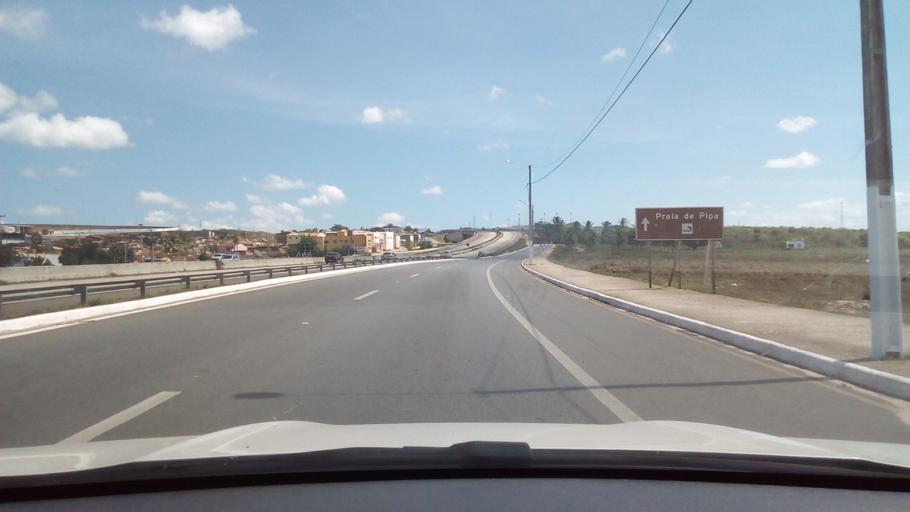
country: BR
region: Rio Grande do Norte
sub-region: Goianinha
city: Goianinha
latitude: -6.2721
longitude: -35.2082
